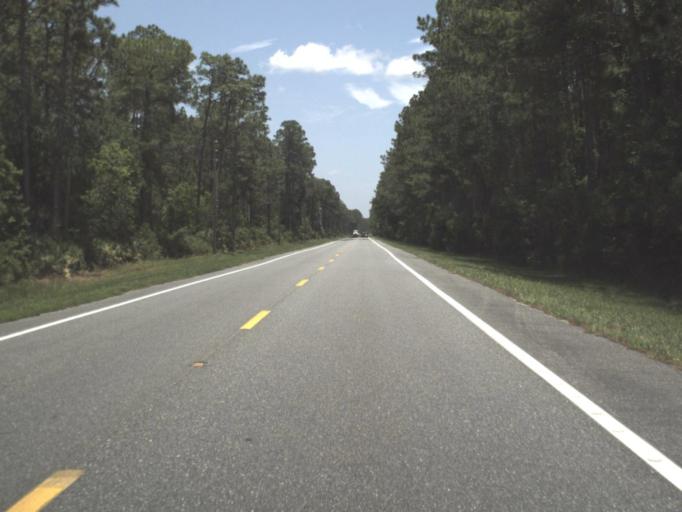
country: US
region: Florida
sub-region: Levy County
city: Williston Highlands
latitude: 29.1971
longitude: -82.6120
